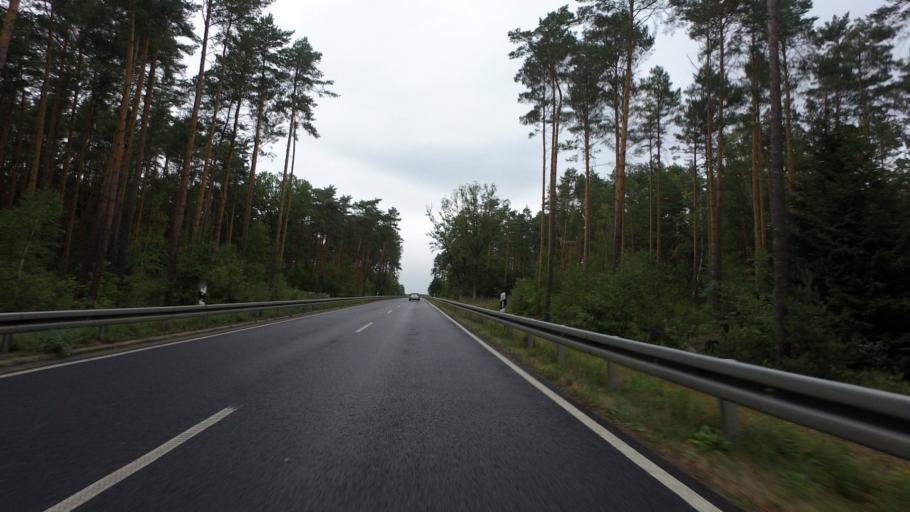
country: DE
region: Saxony
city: Bernsdorf
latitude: 51.3631
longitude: 14.0806
